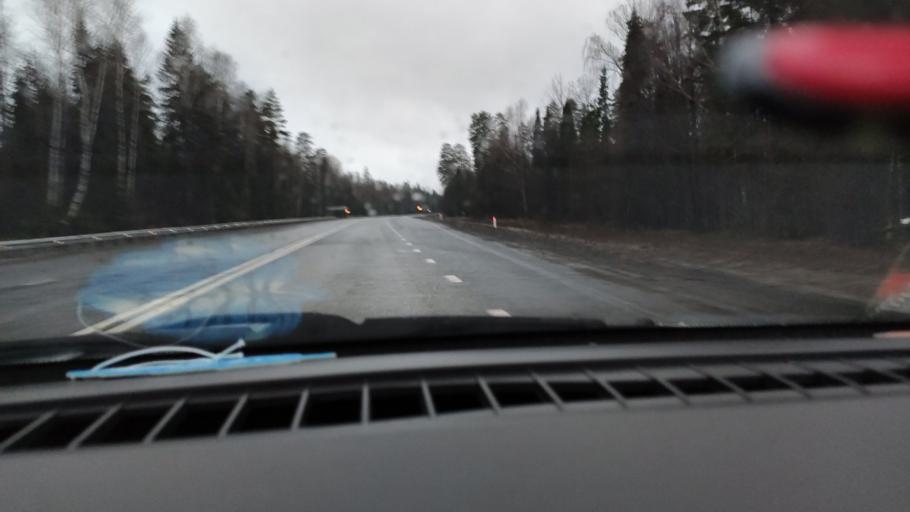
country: RU
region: Udmurtiya
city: Alnashi
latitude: 56.0893
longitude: 52.4412
